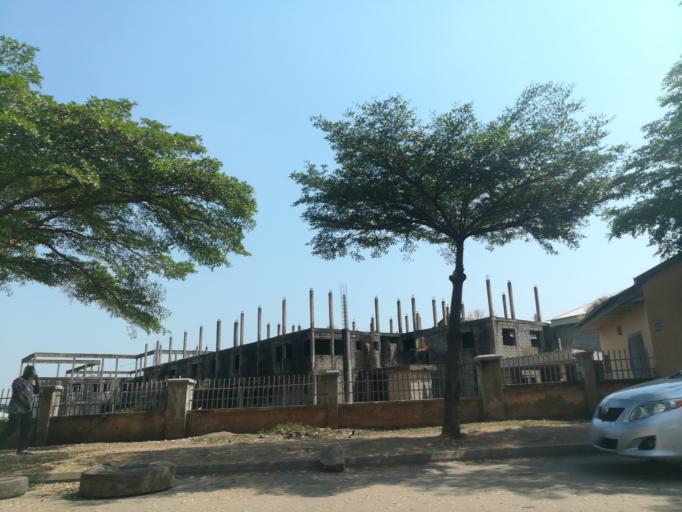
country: NG
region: Abuja Federal Capital Territory
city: Abuja
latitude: 9.0694
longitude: 7.4436
